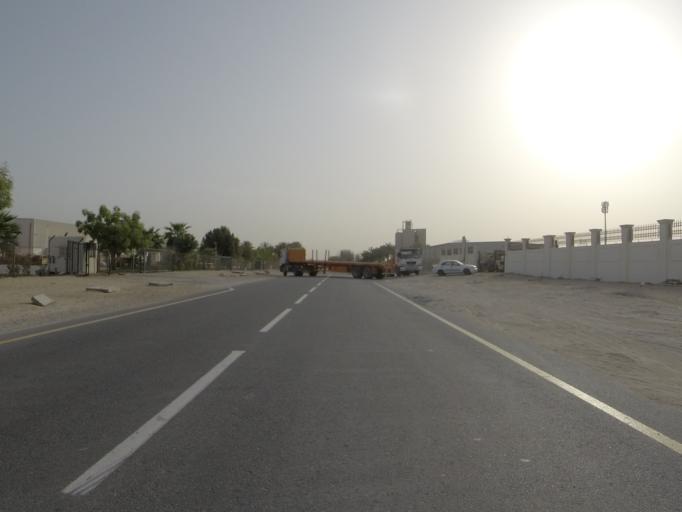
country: AE
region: Dubai
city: Dubai
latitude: 24.9547
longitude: 55.0609
